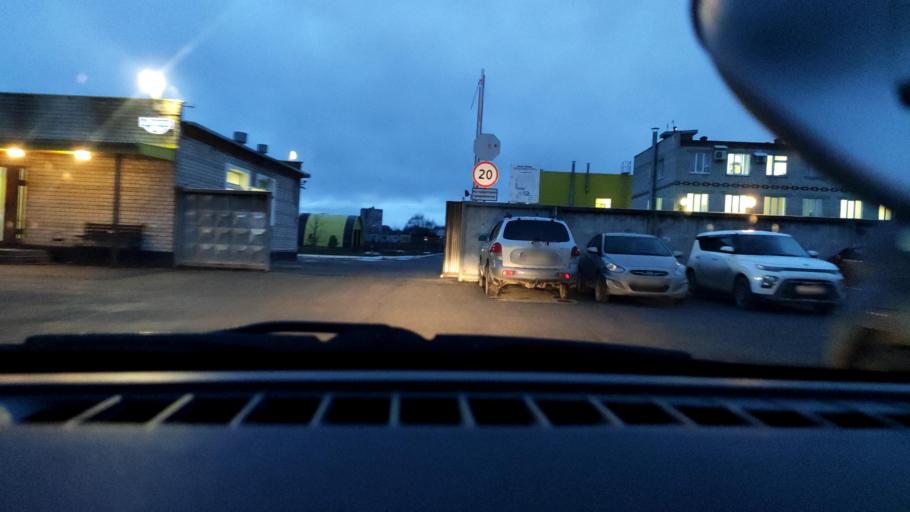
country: RU
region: Perm
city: Kondratovo
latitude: 57.9536
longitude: 56.1727
